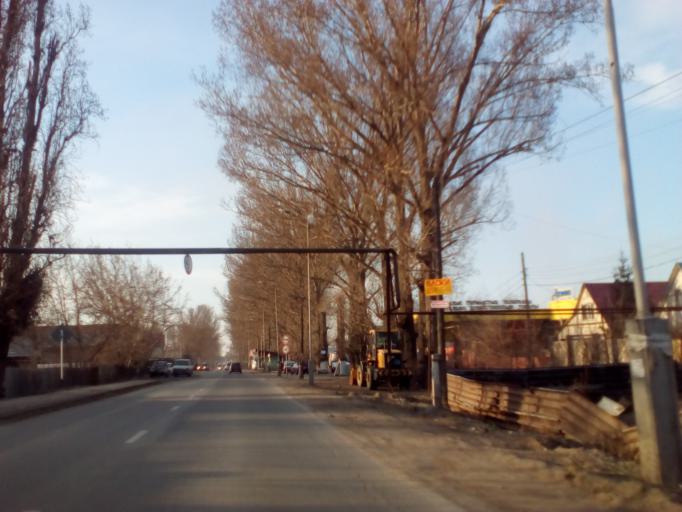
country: KZ
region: Almaty Oblysy
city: Burunday
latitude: 43.2531
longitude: 76.7829
